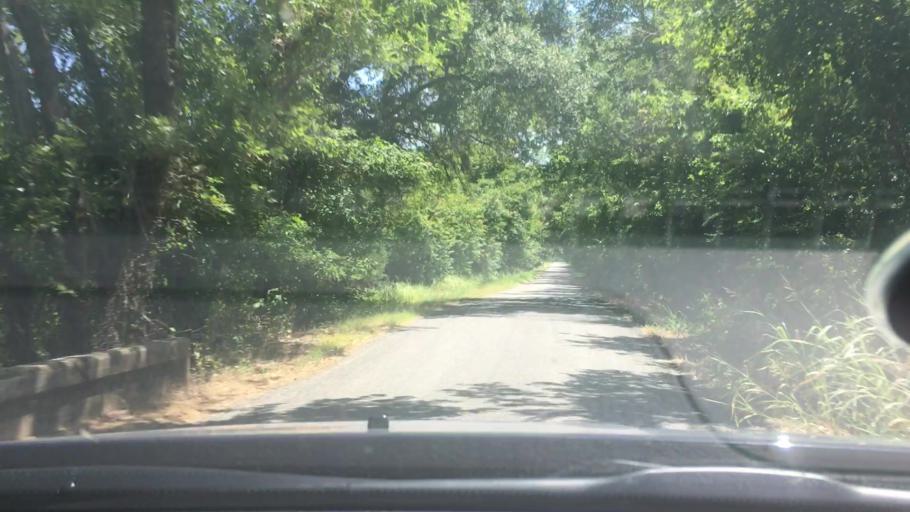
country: US
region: Oklahoma
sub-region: Bryan County
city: Durant
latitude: 33.9830
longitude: -96.2624
